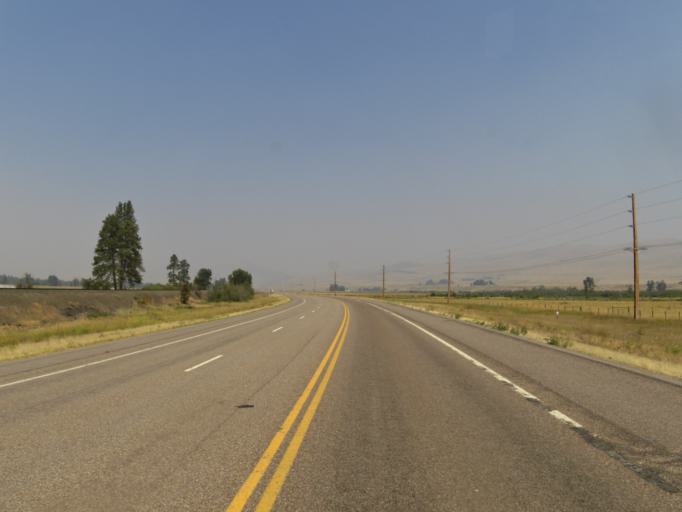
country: US
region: Montana
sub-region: Missoula County
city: Frenchtown
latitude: 47.1976
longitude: -114.1054
